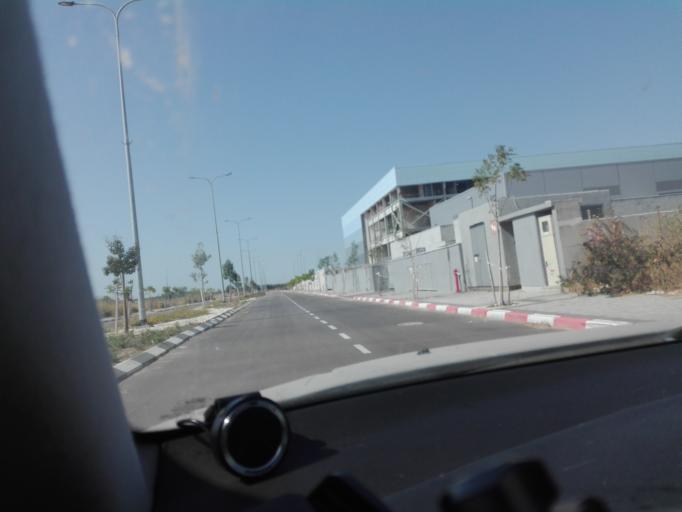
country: IL
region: Central District
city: Bene 'Ayish
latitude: 31.7241
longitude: 34.7579
